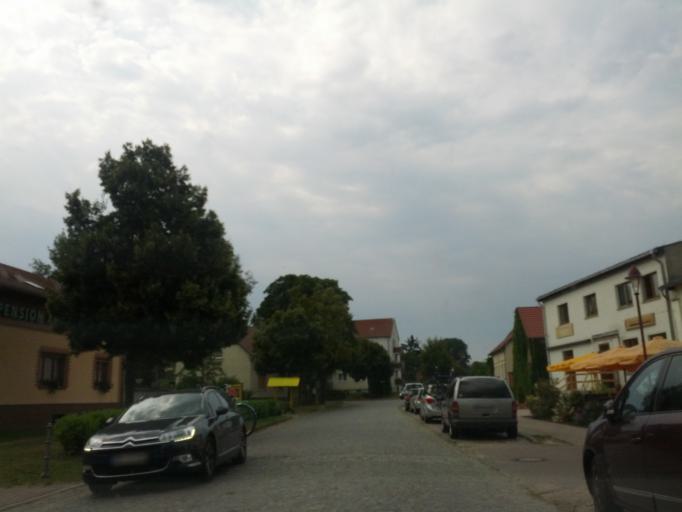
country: DE
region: Brandenburg
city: Fehrbellin
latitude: 52.7590
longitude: 12.8765
